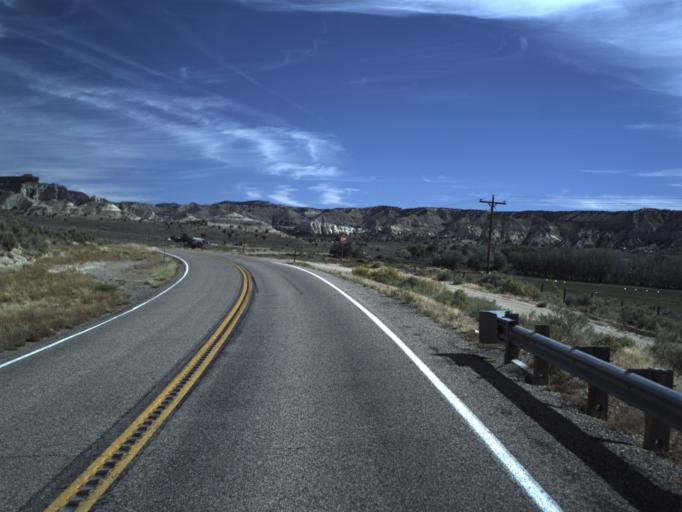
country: US
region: Utah
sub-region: Garfield County
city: Panguitch
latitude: 37.5592
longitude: -112.0177
